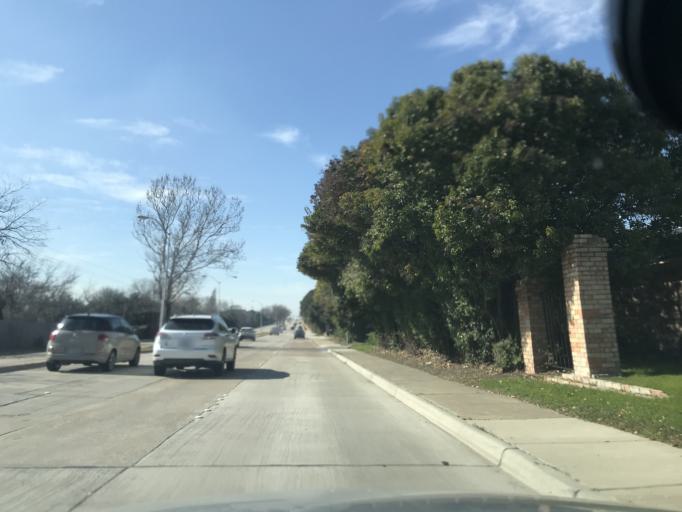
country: US
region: Texas
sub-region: Collin County
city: Plano
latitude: 33.0412
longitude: -96.7572
